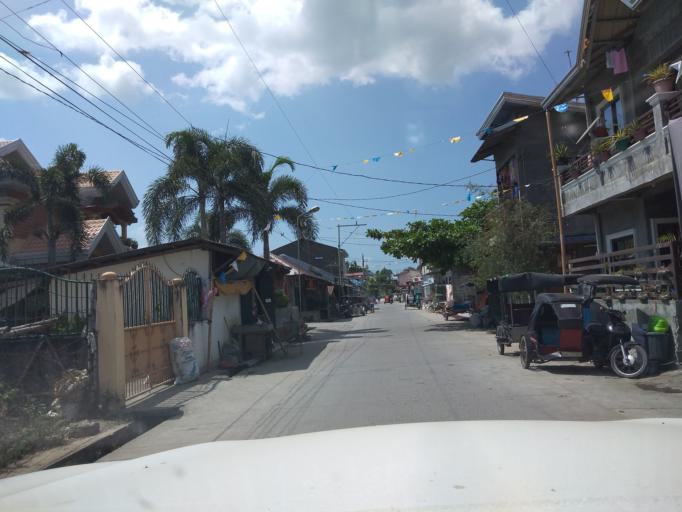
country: PH
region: Central Luzon
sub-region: Province of Pampanga
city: Bahay Pare
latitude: 15.0327
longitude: 120.8794
